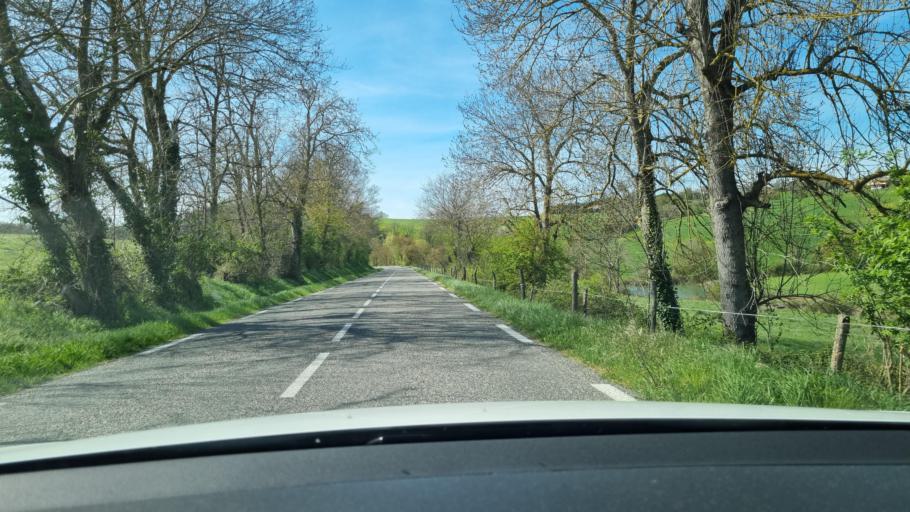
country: FR
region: Midi-Pyrenees
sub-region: Departement du Gers
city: Samatan
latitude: 43.4922
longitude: 1.0023
